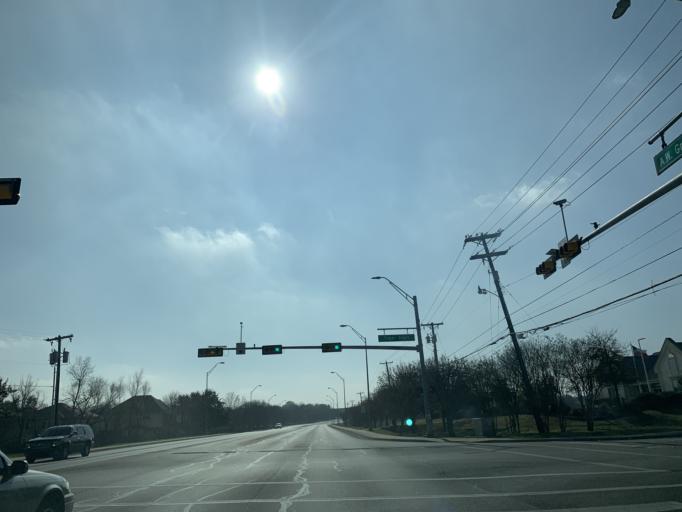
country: US
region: Texas
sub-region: Williamson County
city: Round Rock
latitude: 30.5323
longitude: -97.6522
